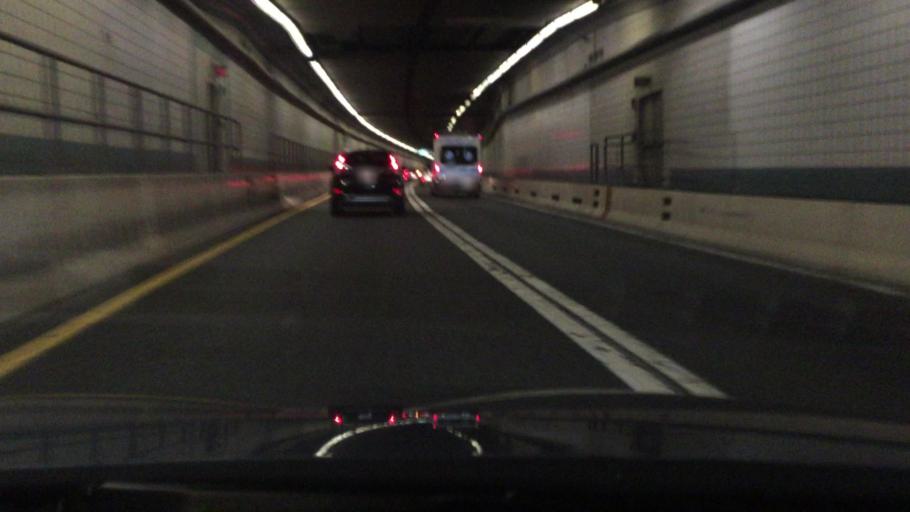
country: US
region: Massachusetts
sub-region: Suffolk County
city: South Boston
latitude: 42.3509
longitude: -71.0389
